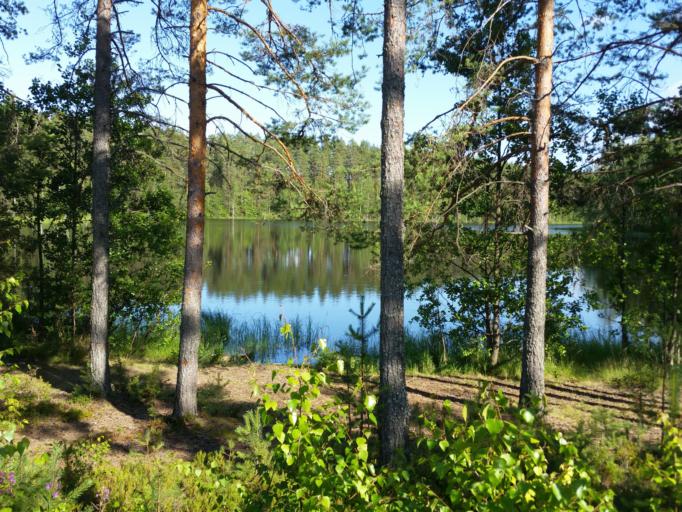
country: FI
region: Southern Savonia
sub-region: Savonlinna
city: Sulkava
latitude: 61.7773
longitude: 28.4218
